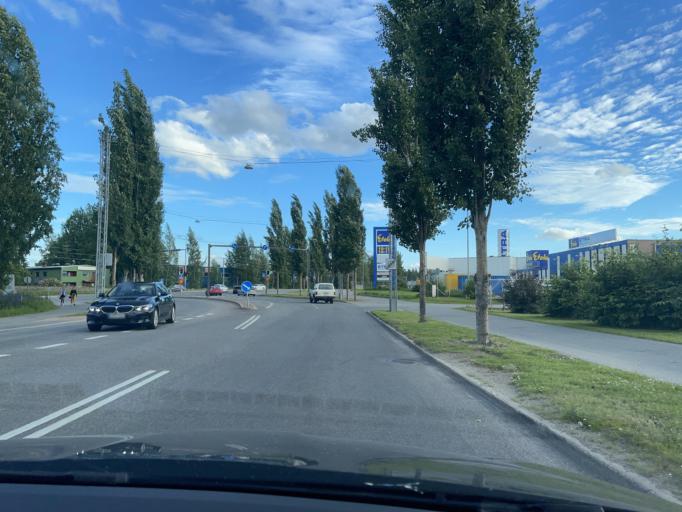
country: FI
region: Central Finland
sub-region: Jyvaeskylae
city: Jyvaeskylae
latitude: 62.2548
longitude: 25.7769
